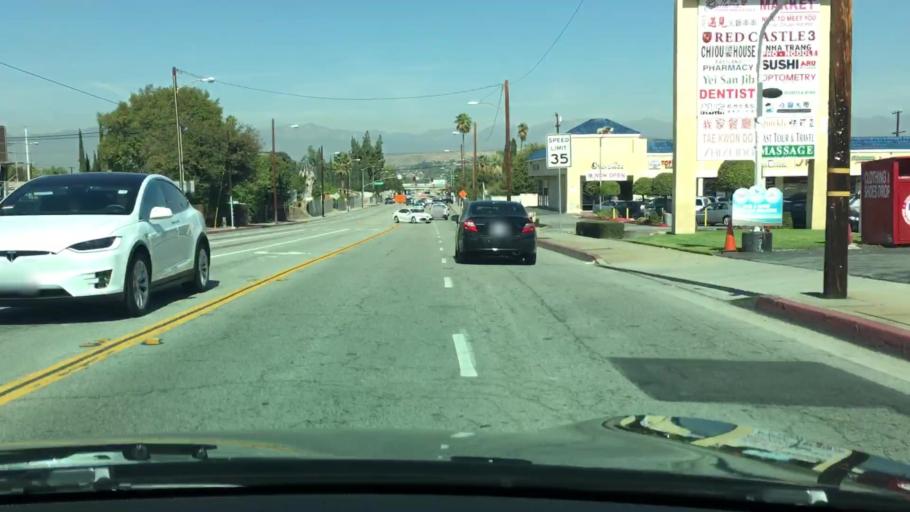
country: US
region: California
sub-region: Los Angeles County
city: Rowland Heights
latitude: 33.9887
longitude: -117.9056
